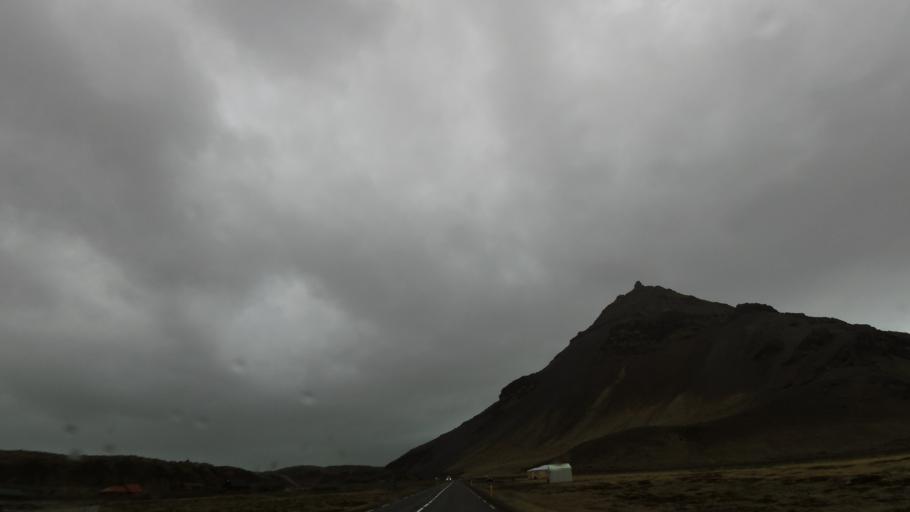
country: IS
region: West
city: Olafsvik
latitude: 64.7666
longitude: -23.6376
